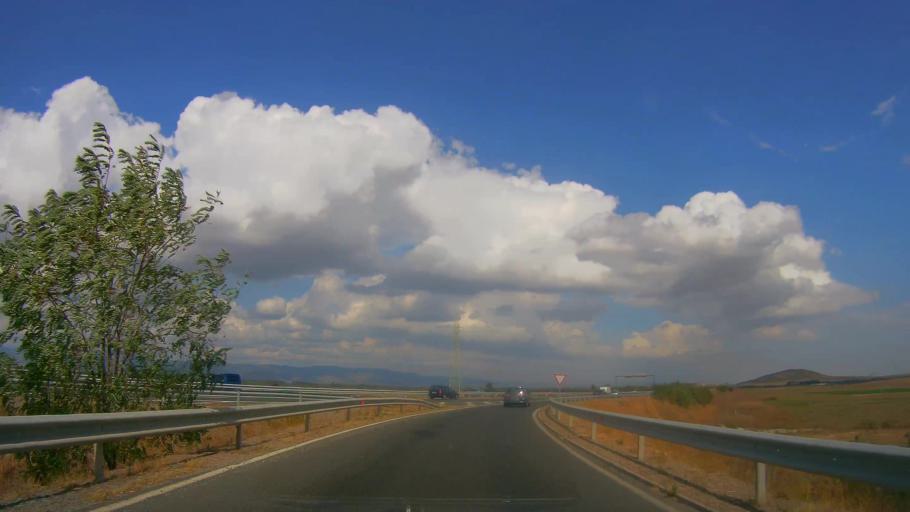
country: BG
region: Yambol
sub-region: Obshtina Yambol
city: Yambol
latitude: 42.5379
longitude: 26.4213
